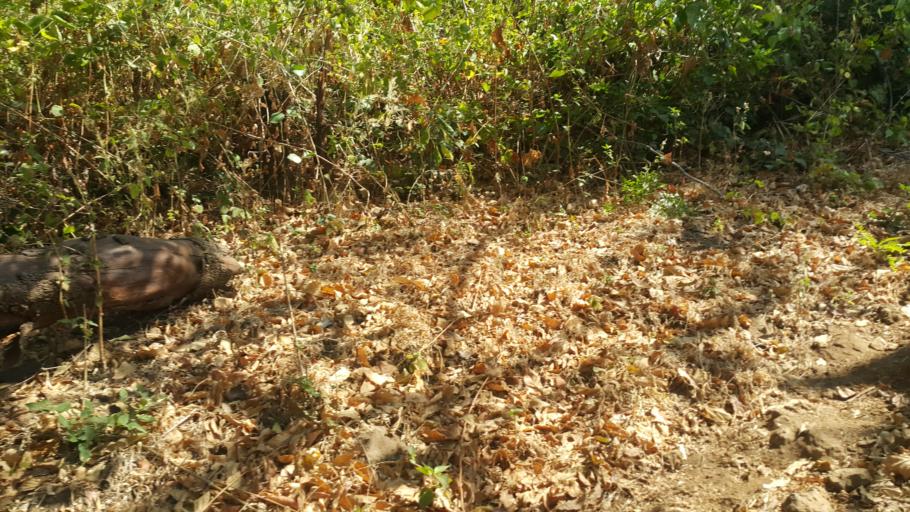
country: NI
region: Leon
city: Telica
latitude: 12.5923
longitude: -86.8295
